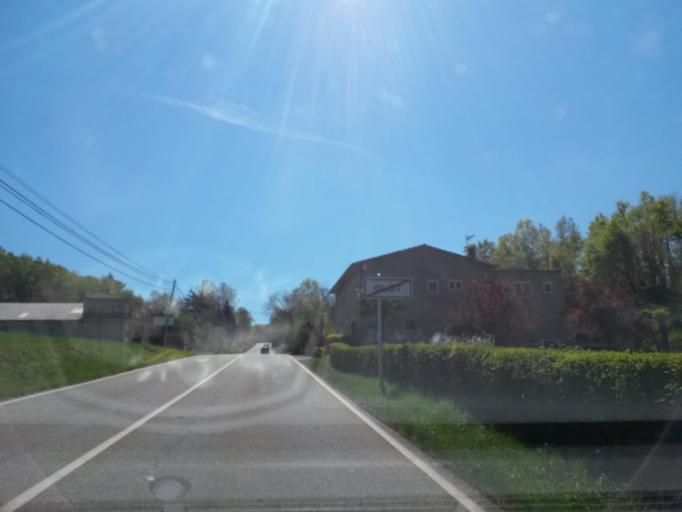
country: ES
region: Catalonia
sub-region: Provincia de Girona
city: Sant Cristofol de les Fonts
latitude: 42.1675
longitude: 2.5045
